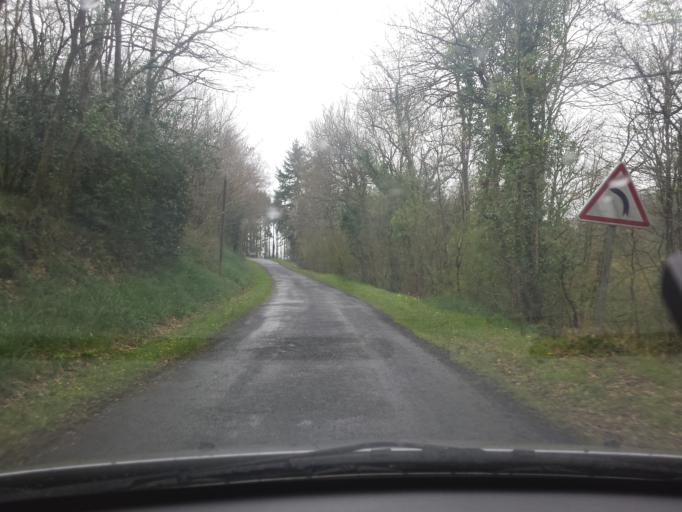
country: FR
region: Pays de la Loire
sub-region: Departement de la Vendee
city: Sainte-Hermine
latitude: 46.5937
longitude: -1.0840
